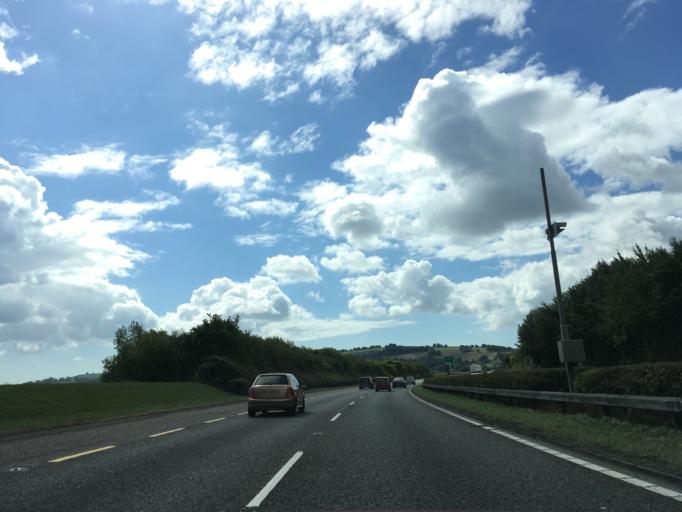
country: IE
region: Munster
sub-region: County Cork
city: Passage West
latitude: 51.8921
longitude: -8.3915
